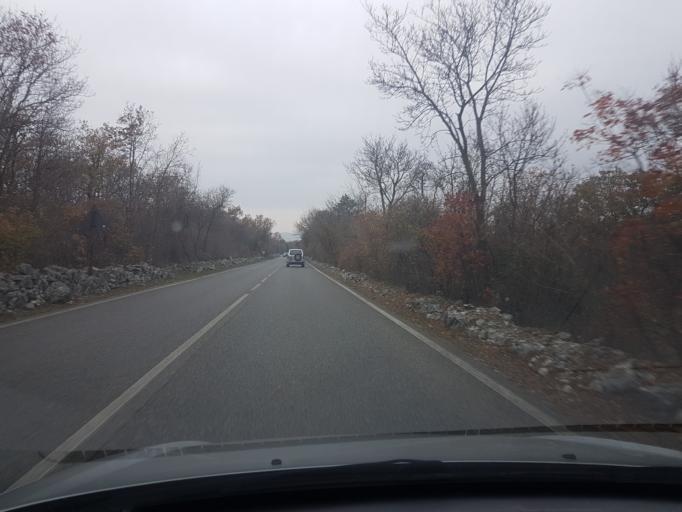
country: IT
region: Friuli Venezia Giulia
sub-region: Provincia di Trieste
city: Santa Croce
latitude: 45.7244
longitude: 13.7146
